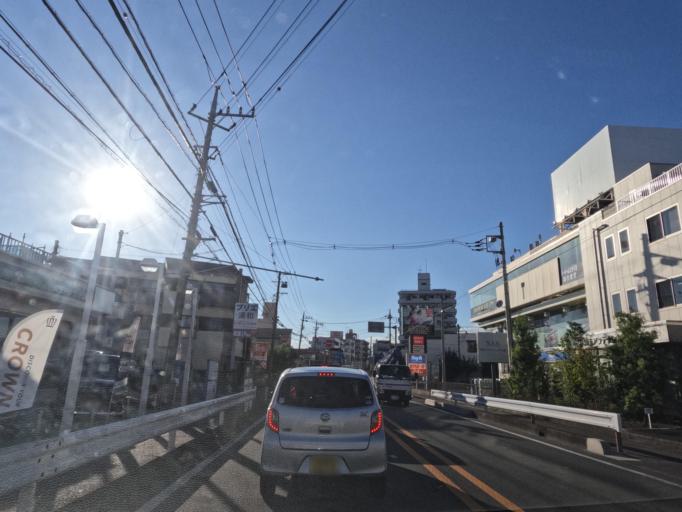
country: JP
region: Saitama
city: Shimotoda
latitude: 35.8530
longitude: 139.6826
